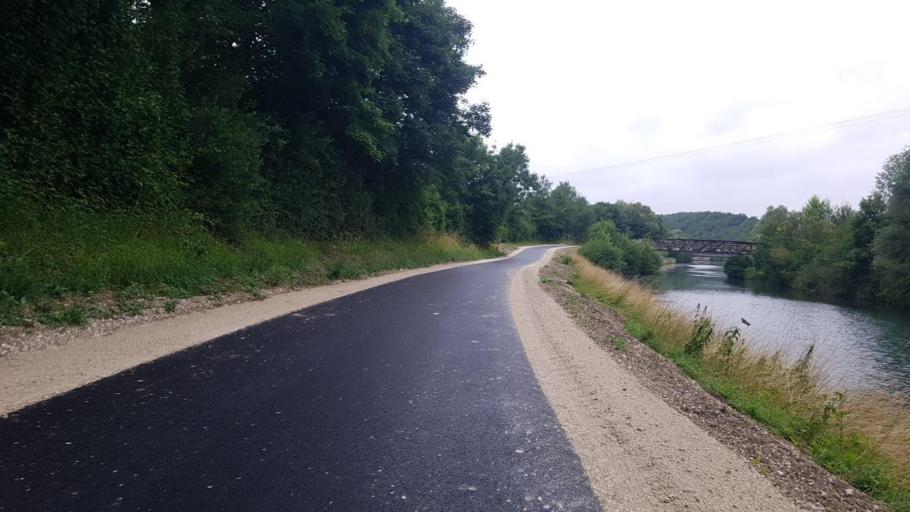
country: FR
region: Champagne-Ardenne
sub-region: Departement de la Marne
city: Vitry-le-Francois
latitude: 48.7621
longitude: 4.5624
